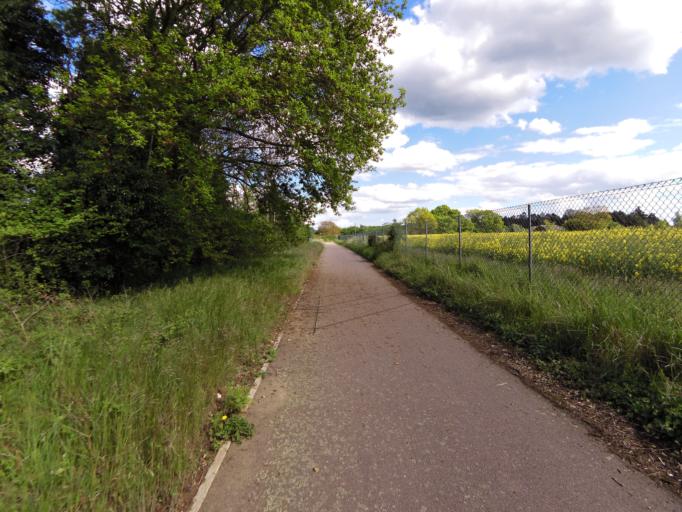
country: GB
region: England
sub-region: Suffolk
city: Great Barton
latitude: 52.2480
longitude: 0.7788
